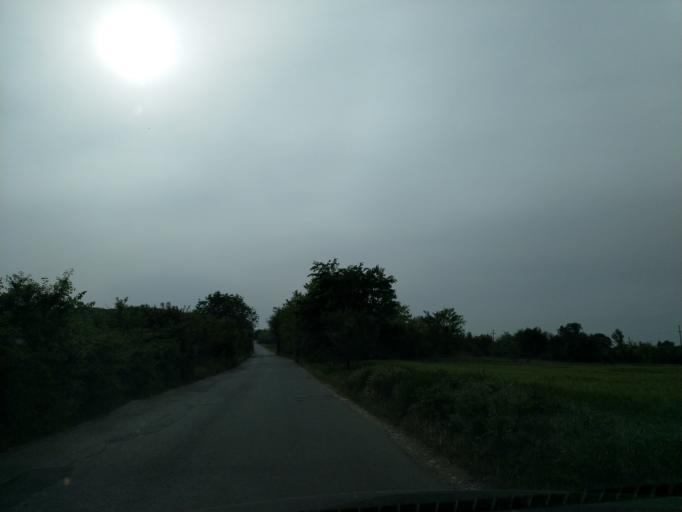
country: RS
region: Central Serbia
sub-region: Pomoravski Okrug
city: Jagodina
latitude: 43.9733
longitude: 21.2150
